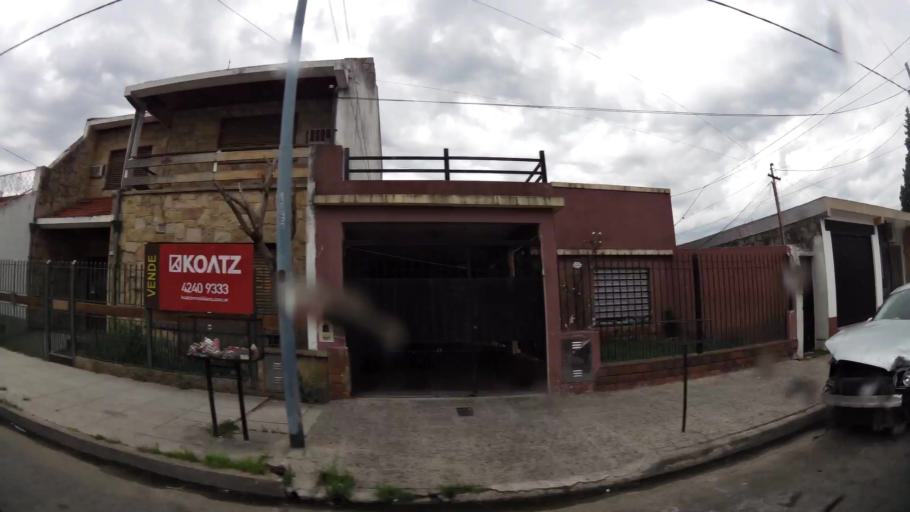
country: AR
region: Buenos Aires
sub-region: Partido de Lanus
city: Lanus
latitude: -34.6873
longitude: -58.4035
